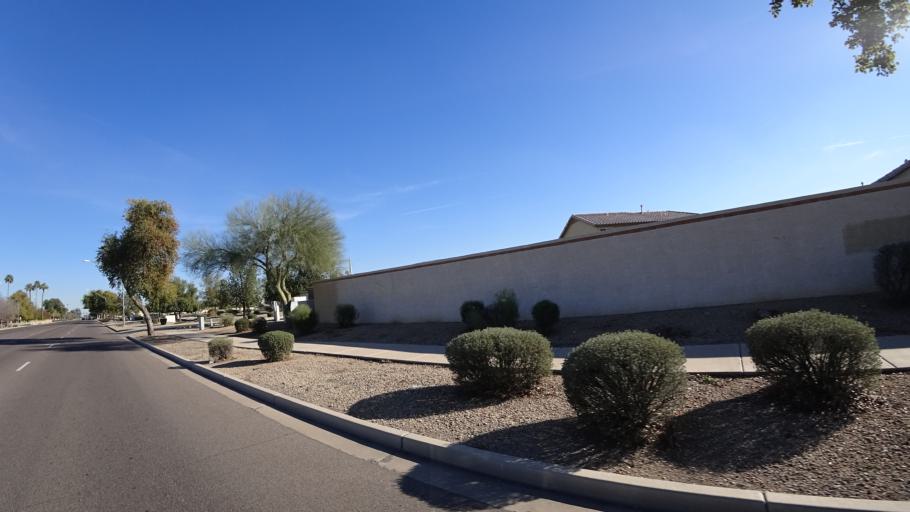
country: US
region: Arizona
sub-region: Maricopa County
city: Glendale
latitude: 33.5232
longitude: -112.2320
